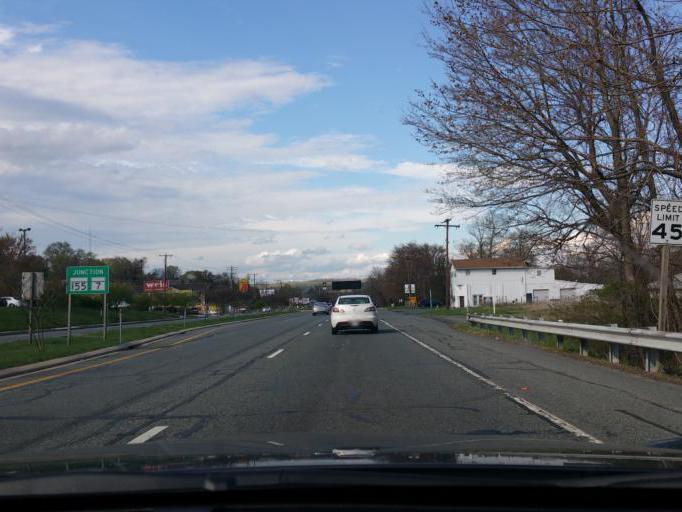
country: US
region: Maryland
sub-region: Harford County
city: Havre de Grace
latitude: 39.5473
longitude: -76.1059
